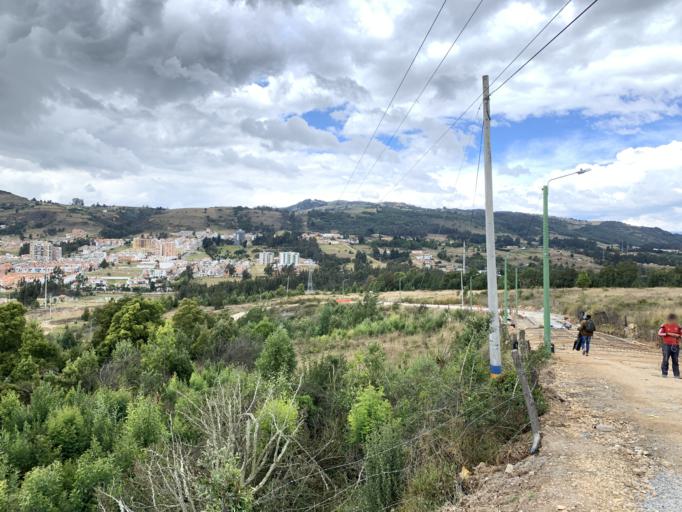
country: CO
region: Boyaca
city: Tunja
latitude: 5.5695
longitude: -73.3270
